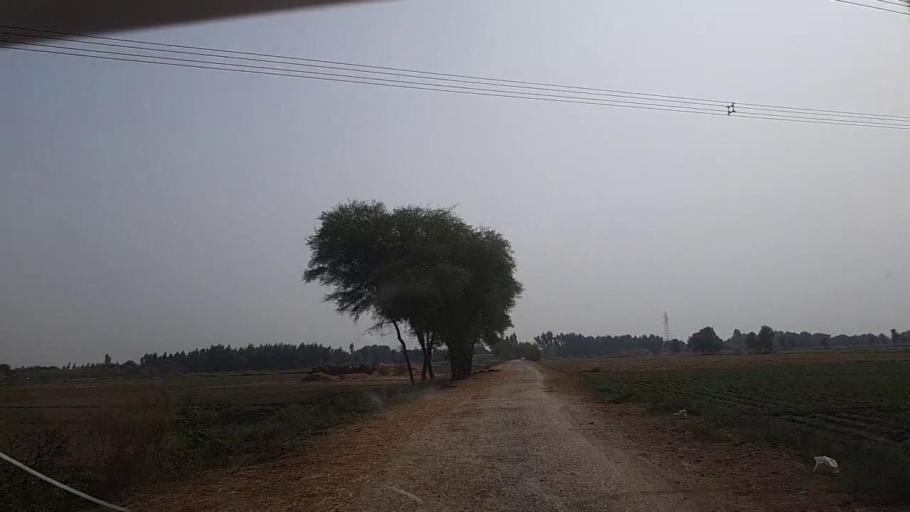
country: PK
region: Sindh
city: Madeji
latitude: 27.7381
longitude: 68.4357
